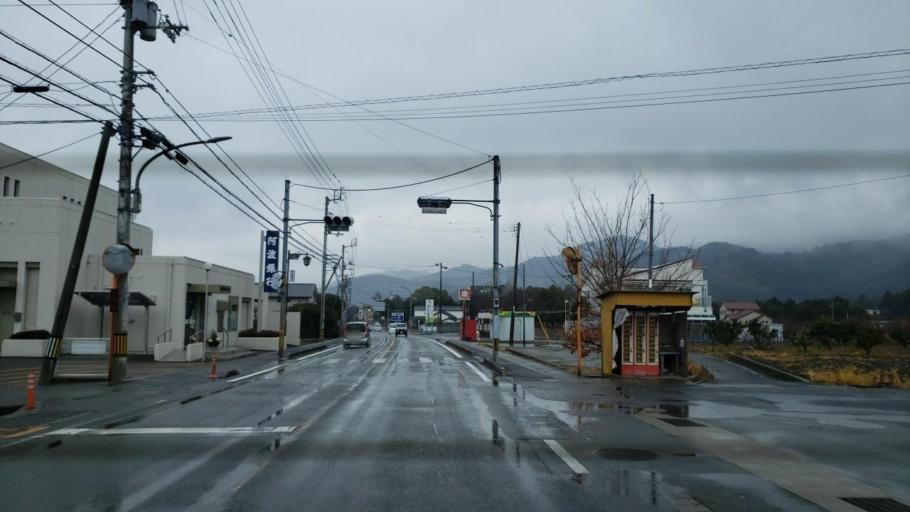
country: JP
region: Tokushima
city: Tokushima-shi
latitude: 34.1588
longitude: 134.5055
